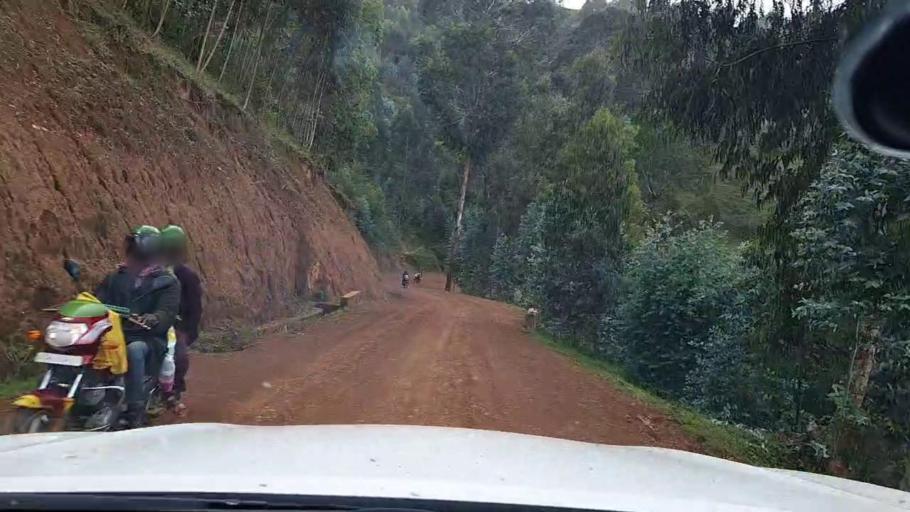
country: RW
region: Western Province
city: Kibuye
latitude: -2.1709
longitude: 29.4360
